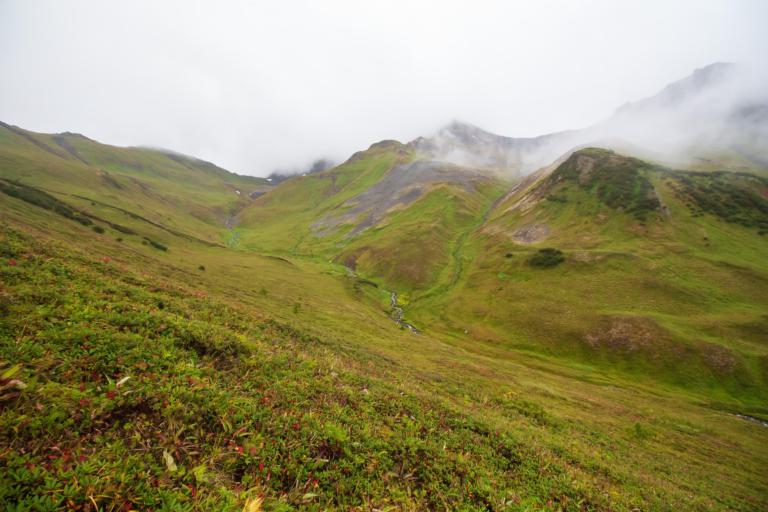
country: RU
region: Kamtsjatka
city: Yelizovo
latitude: 53.9723
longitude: 158.0884
